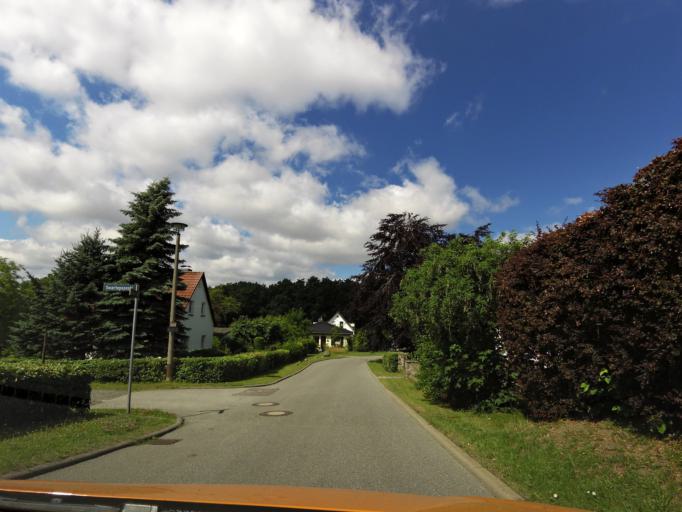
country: DE
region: Mecklenburg-Vorpommern
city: Plau am See
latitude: 53.4397
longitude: 12.2830
